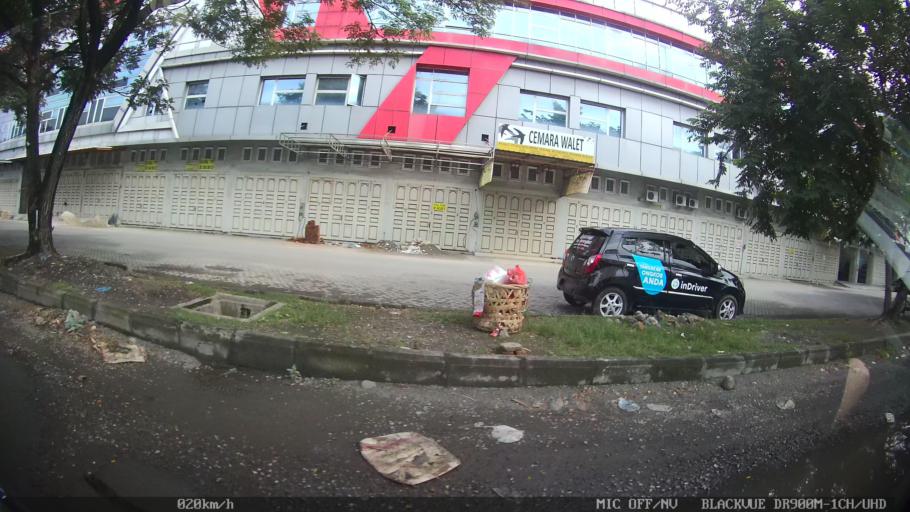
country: ID
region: North Sumatra
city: Medan
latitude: 3.6311
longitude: 98.6977
